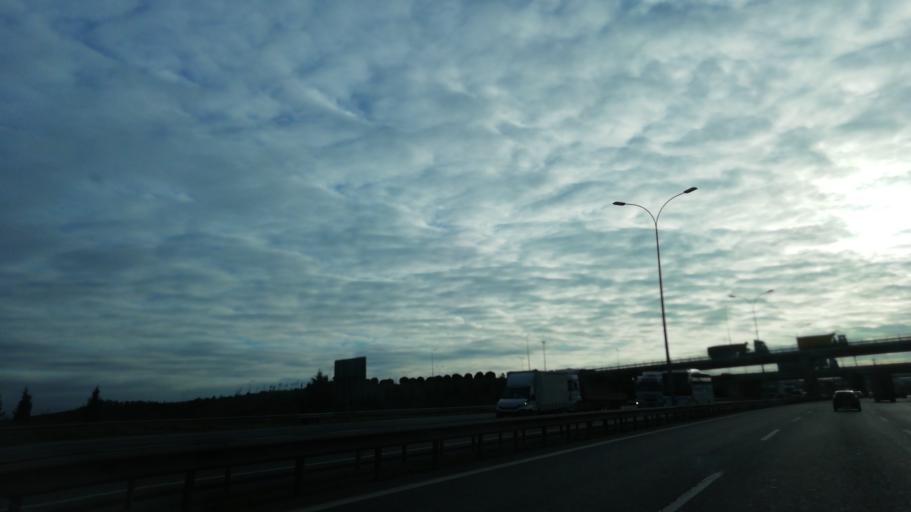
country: TR
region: Istanbul
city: Sultanbeyli
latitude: 40.9313
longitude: 29.3440
